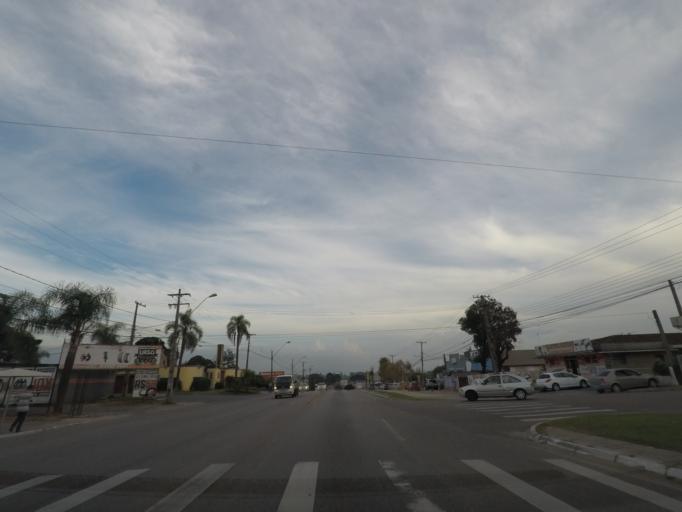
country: BR
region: Parana
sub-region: Colombo
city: Colombo
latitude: -25.3564
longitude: -49.2193
